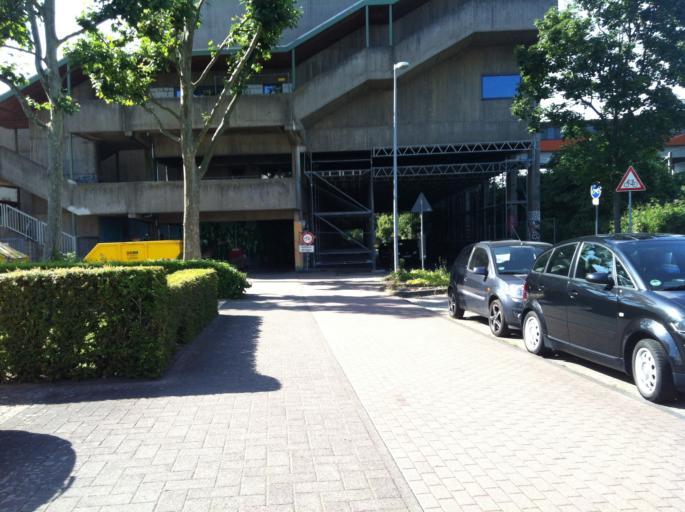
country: DE
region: North Rhine-Westphalia
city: Wesseling
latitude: 50.8252
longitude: 6.9742
